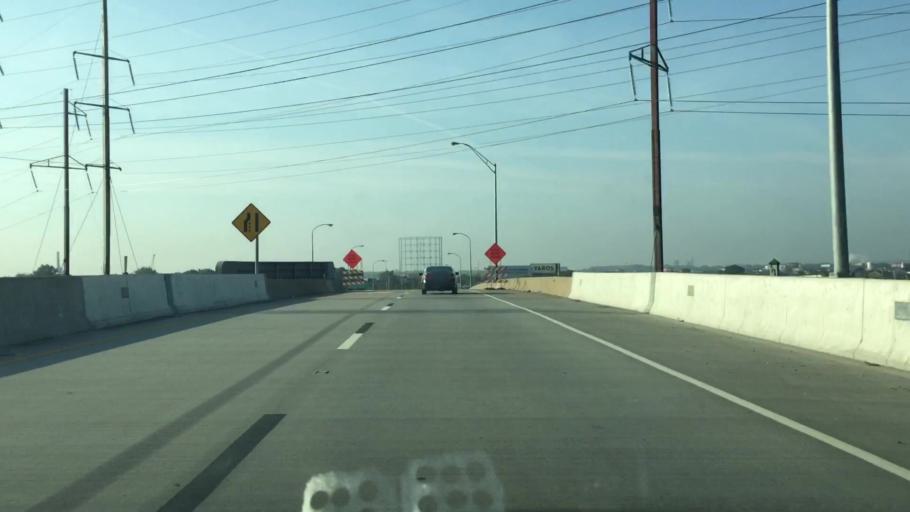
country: US
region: New Jersey
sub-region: Camden County
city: Pennsauken
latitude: 39.9970
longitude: -75.0843
